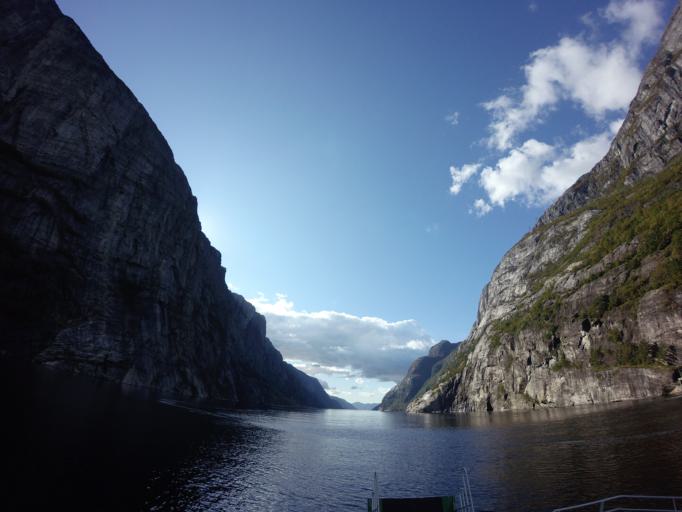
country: NO
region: Vest-Agder
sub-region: Sirdal
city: Tonstad
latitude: 59.0497
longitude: 6.6195
